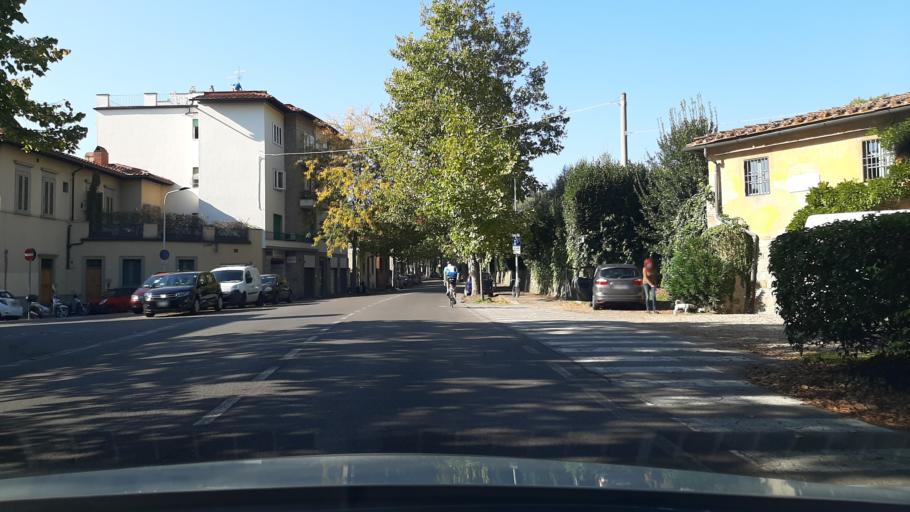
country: IT
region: Tuscany
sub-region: Province of Florence
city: Fiesole
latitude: 43.7859
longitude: 11.2878
